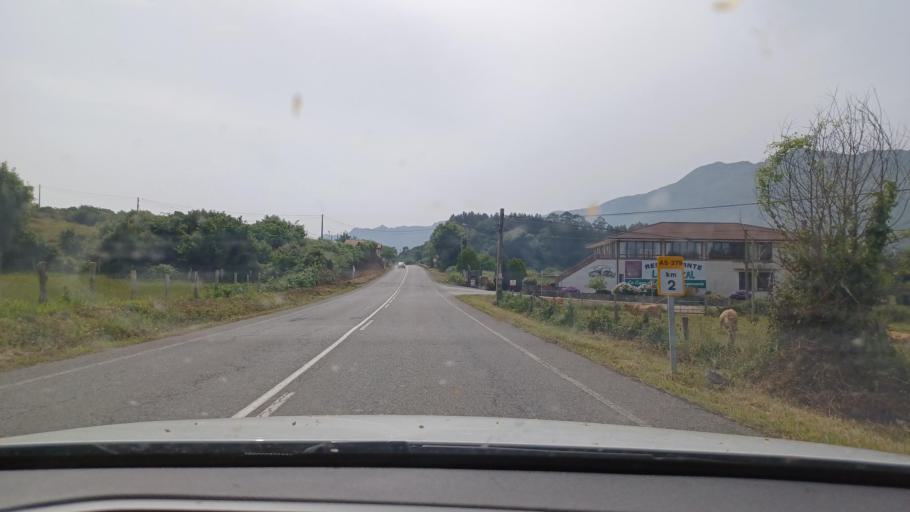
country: ES
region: Asturias
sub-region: Province of Asturias
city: Ribadesella
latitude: 43.4570
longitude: -5.0419
